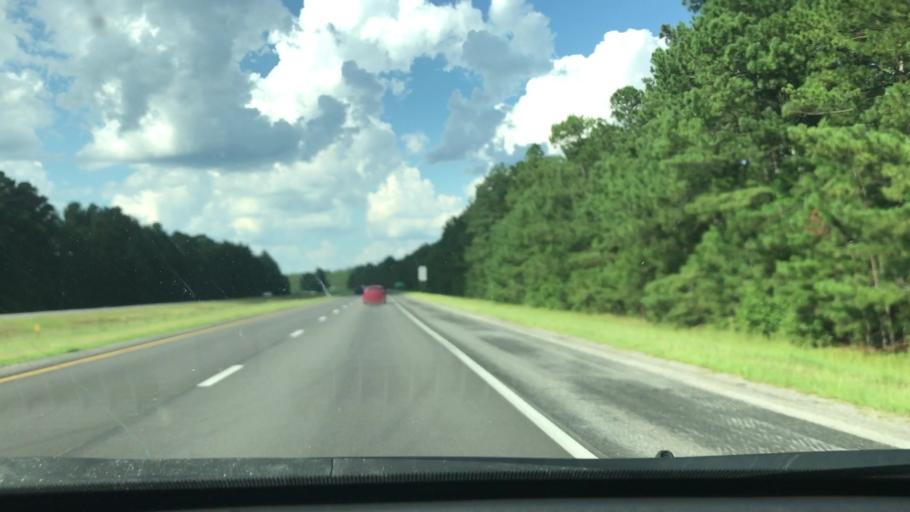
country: US
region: South Carolina
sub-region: Sumter County
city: East Sumter
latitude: 33.8680
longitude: -80.1073
